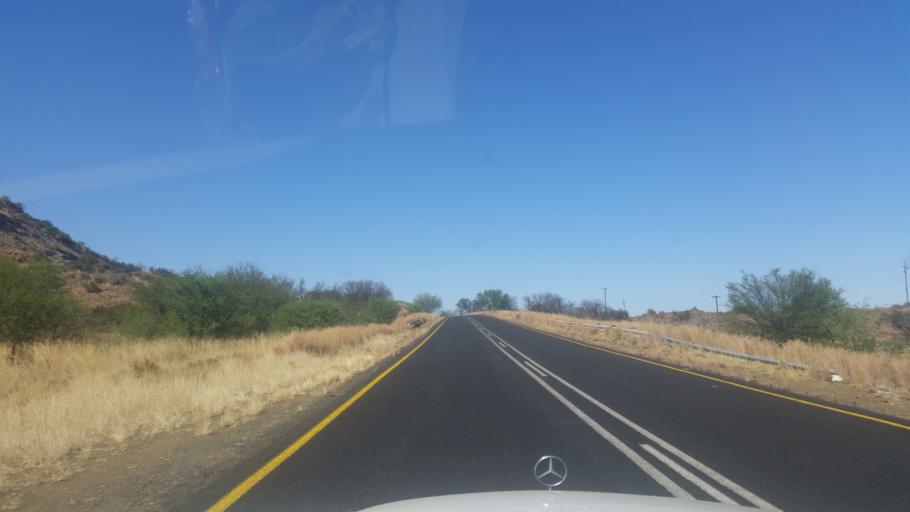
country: ZA
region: Orange Free State
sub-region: Xhariep District Municipality
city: Trompsburg
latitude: -30.5171
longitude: 26.0236
